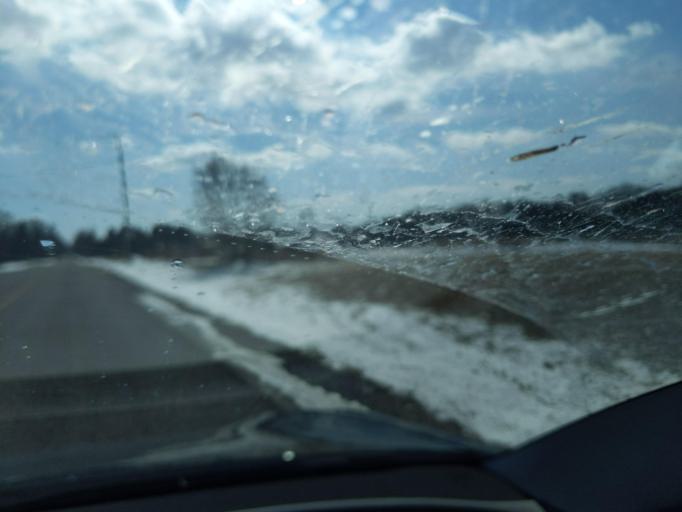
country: US
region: Michigan
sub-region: Livingston County
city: Fowlerville
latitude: 42.5850
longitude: -84.0890
